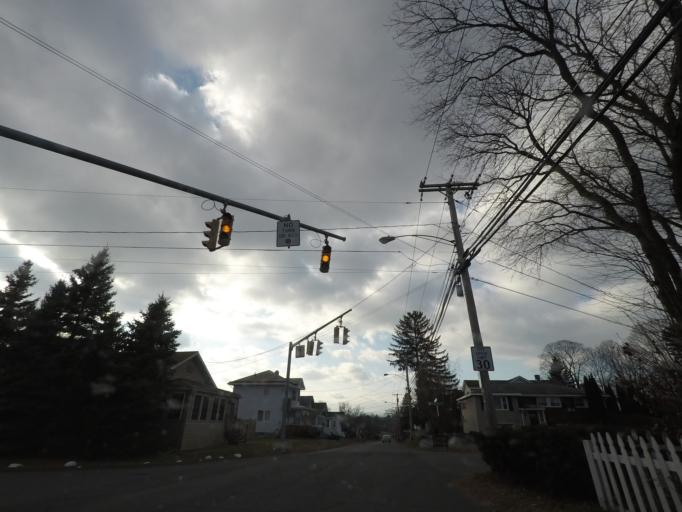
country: US
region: New York
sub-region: Albany County
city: Roessleville
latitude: 42.6723
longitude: -73.8190
